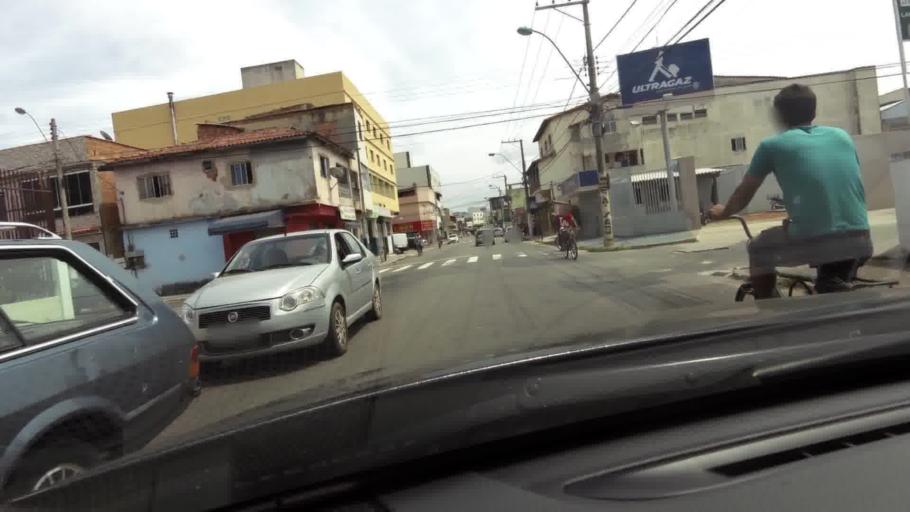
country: BR
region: Espirito Santo
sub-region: Vila Velha
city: Vila Velha
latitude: -20.3420
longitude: -40.3037
